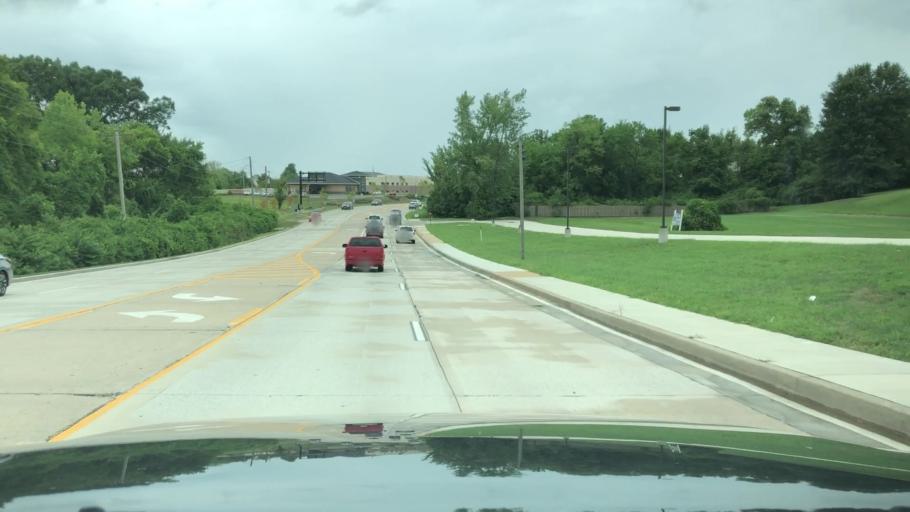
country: US
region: Missouri
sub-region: Saint Charles County
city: Saint Charles
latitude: 38.7704
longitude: -90.5252
